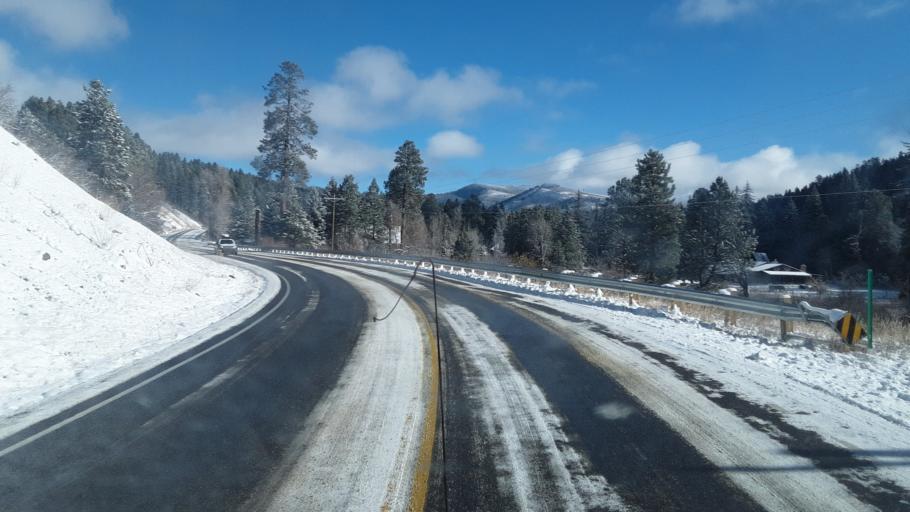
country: US
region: Colorado
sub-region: La Plata County
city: Bayfield
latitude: 37.3463
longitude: -107.6981
